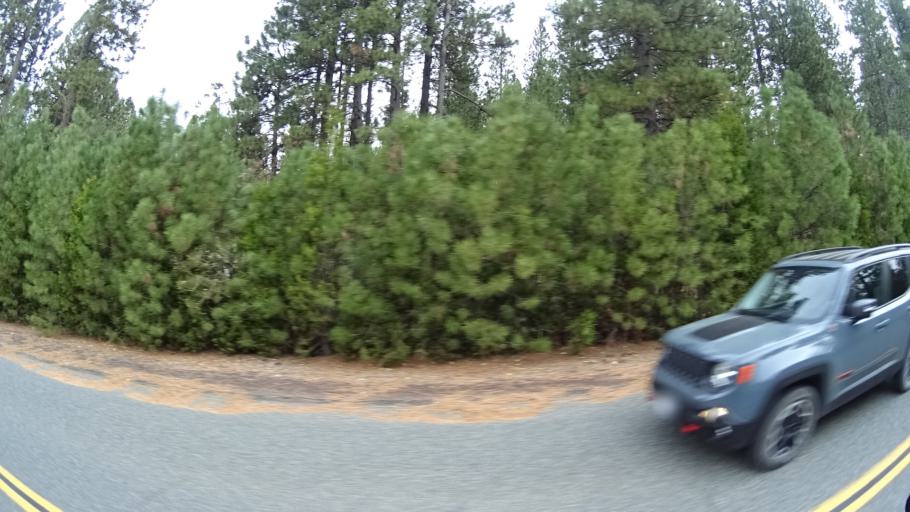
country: US
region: California
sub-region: Siskiyou County
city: Weed
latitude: 41.4095
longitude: -122.3768
